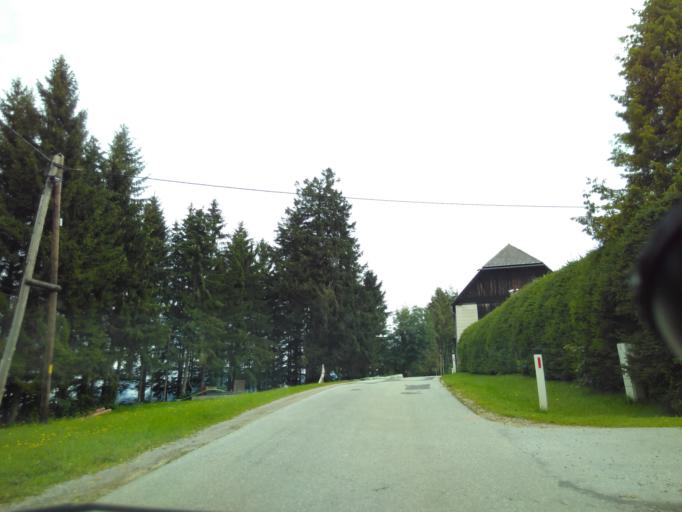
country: AT
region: Styria
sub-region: Politischer Bezirk Graz-Umgebung
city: Semriach
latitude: 47.2541
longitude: 15.4065
